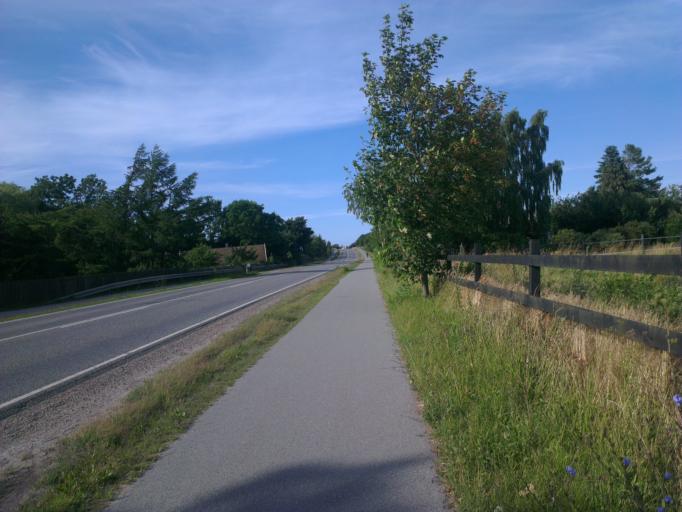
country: DK
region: Capital Region
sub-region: Frederikssund Kommune
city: Skibby
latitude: 55.7641
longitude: 11.9578
